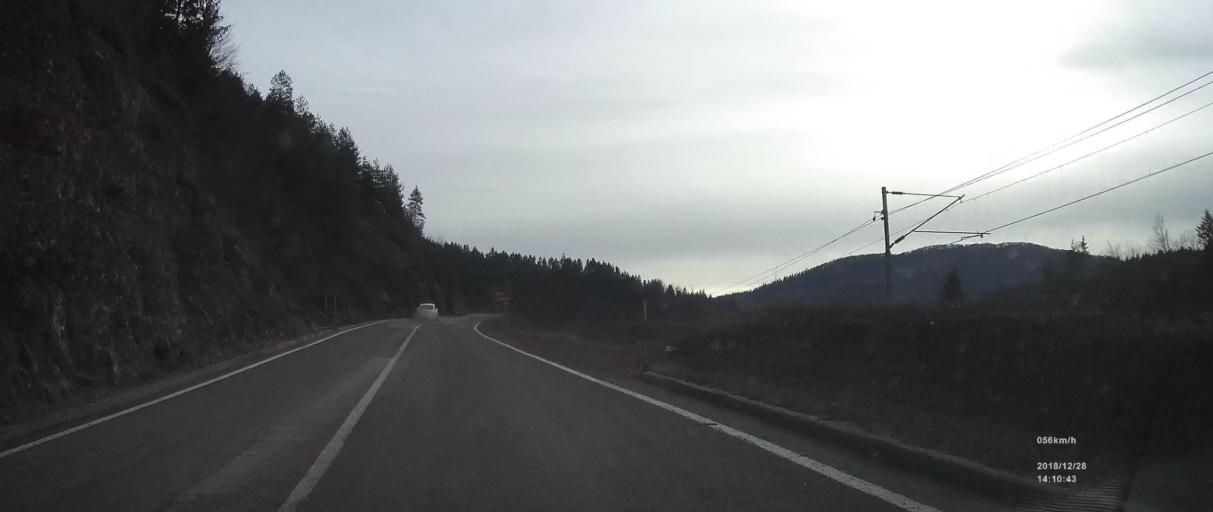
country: SI
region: Kostel
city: Kostel
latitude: 45.4518
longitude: 14.9781
